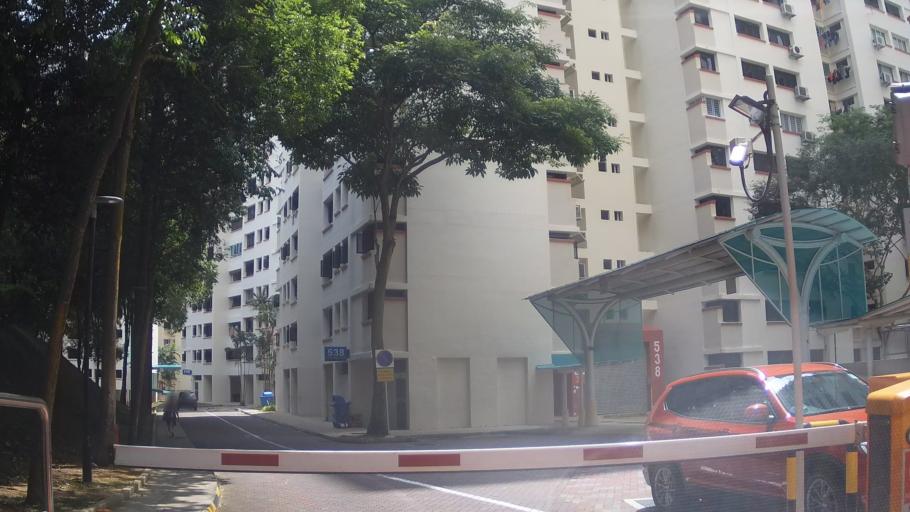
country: MY
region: Johor
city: Johor Bahru
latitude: 1.3842
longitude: 103.7642
